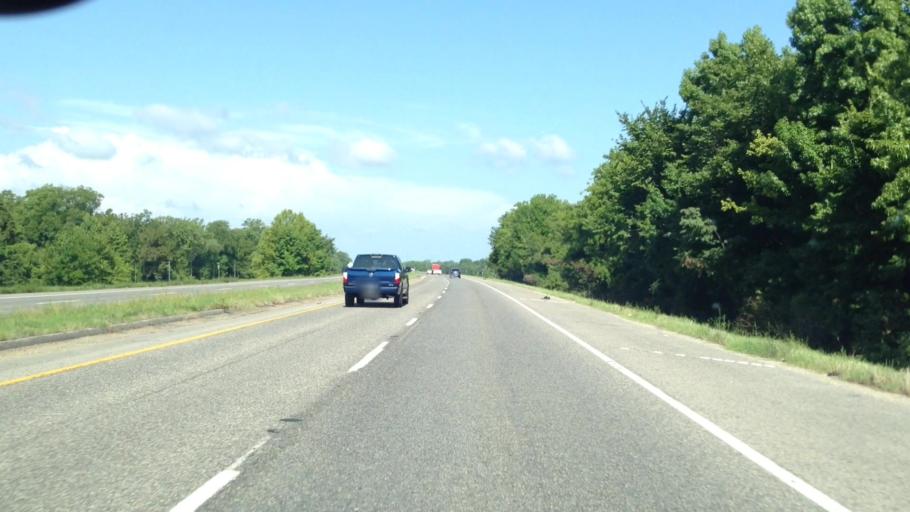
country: US
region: Louisiana
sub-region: Saint Landry Parish
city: Krotz Springs
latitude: 30.5488
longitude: -91.8341
